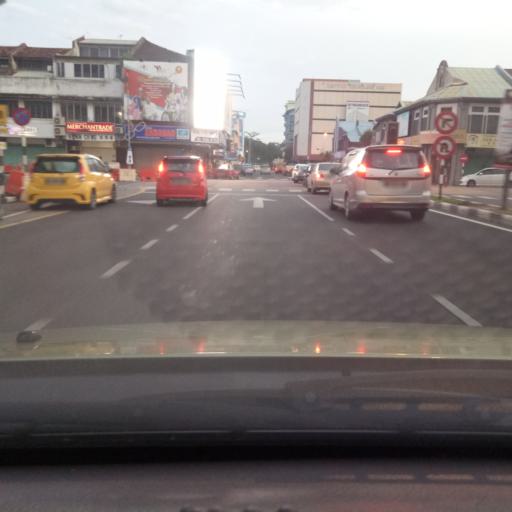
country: MY
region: Kedah
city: Alor Setar
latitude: 6.1176
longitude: 100.3687
